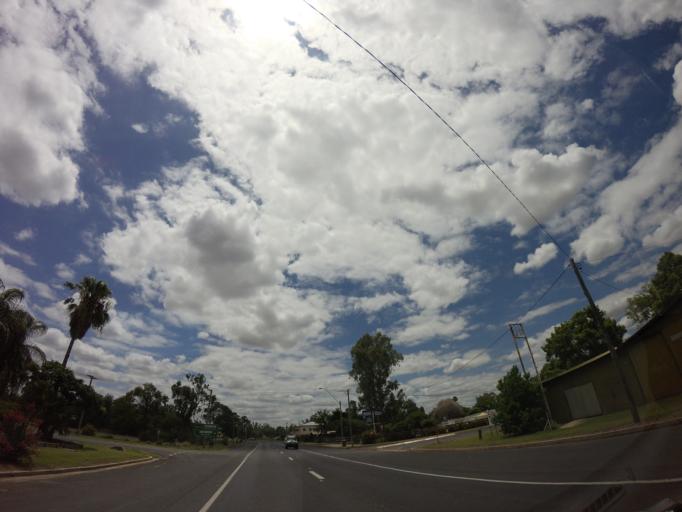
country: AU
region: New South Wales
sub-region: Moree Plains
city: Boggabilla
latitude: -28.6057
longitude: 150.3588
